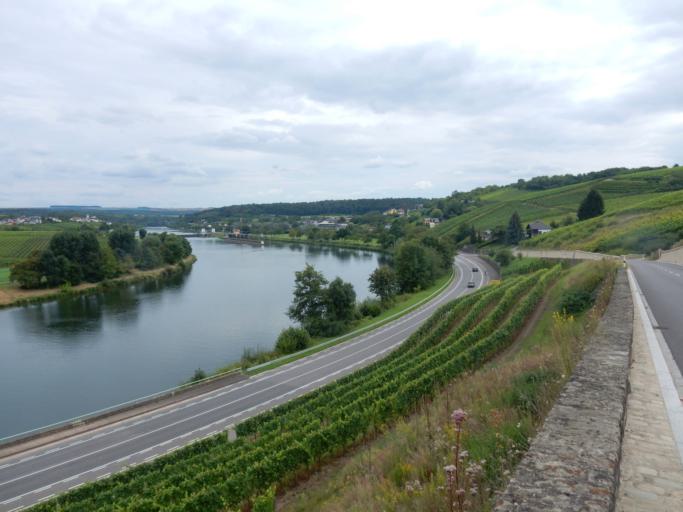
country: DE
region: Rheinland-Pfalz
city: Palzem
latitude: 49.5731
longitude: 6.3561
